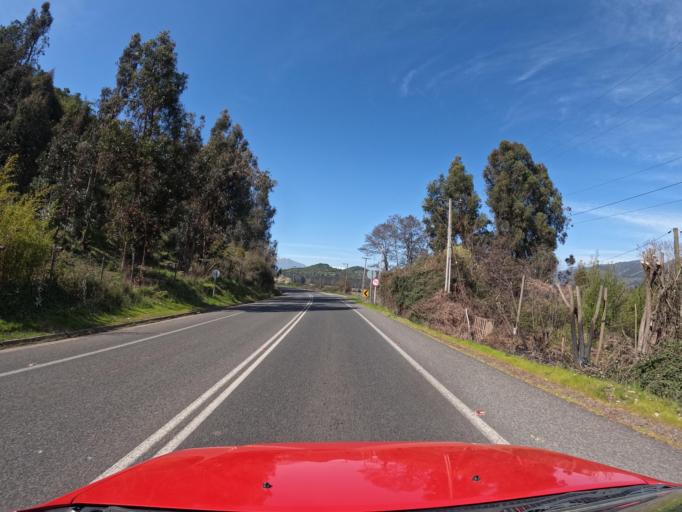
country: CL
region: Maule
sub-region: Provincia de Curico
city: Teno
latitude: -34.9794
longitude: -70.9812
